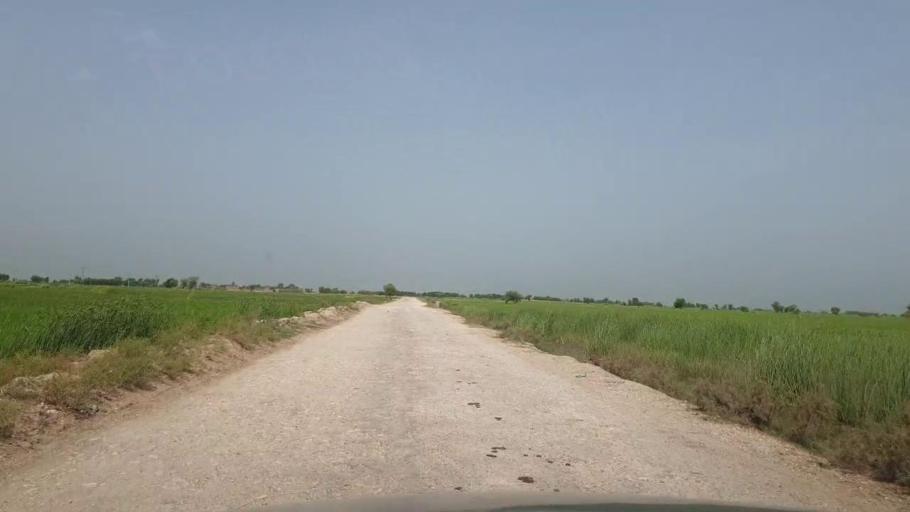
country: PK
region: Sindh
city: Garhi Yasin
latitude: 27.8594
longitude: 68.4083
